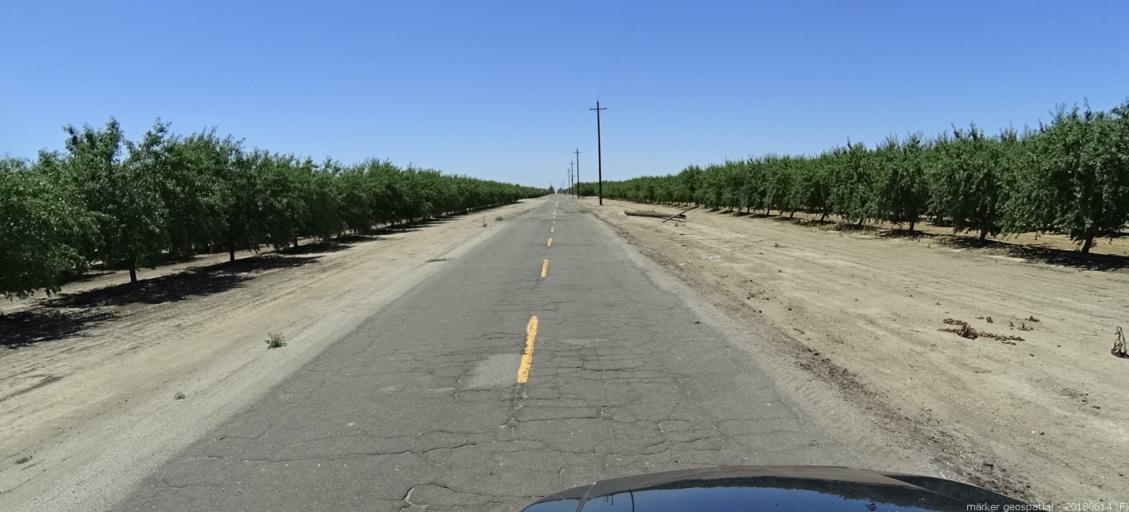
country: US
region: California
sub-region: Madera County
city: Fairmead
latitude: 37.0202
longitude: -120.2744
